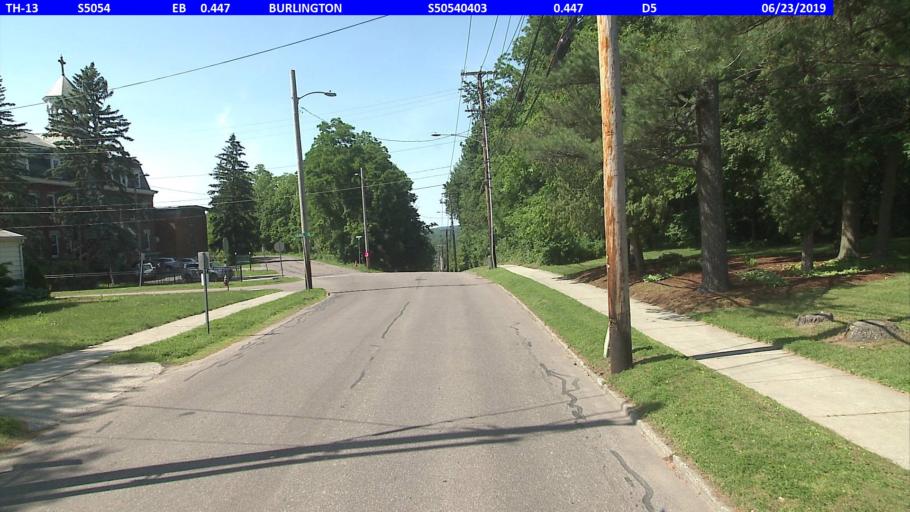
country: US
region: Vermont
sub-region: Chittenden County
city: Burlington
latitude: 44.4871
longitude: -73.2019
